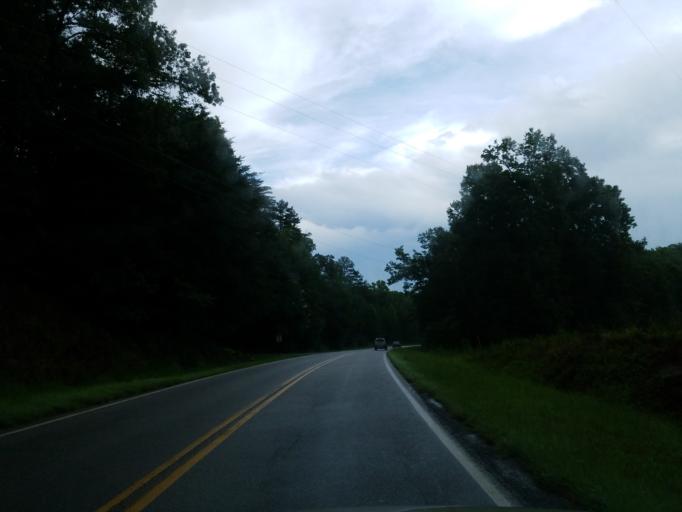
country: US
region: Georgia
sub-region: Lumpkin County
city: Dahlonega
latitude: 34.5329
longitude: -83.9013
